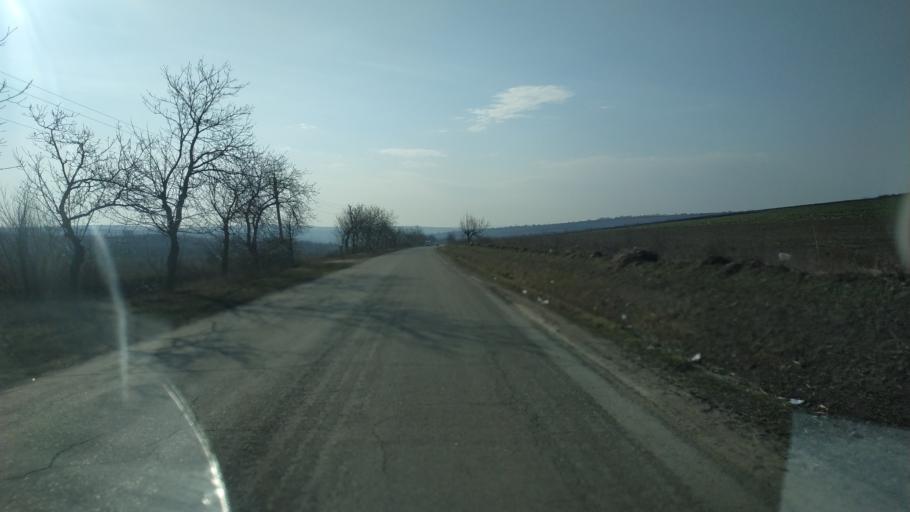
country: MD
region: Chisinau
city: Singera
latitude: 46.8499
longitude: 29.0234
